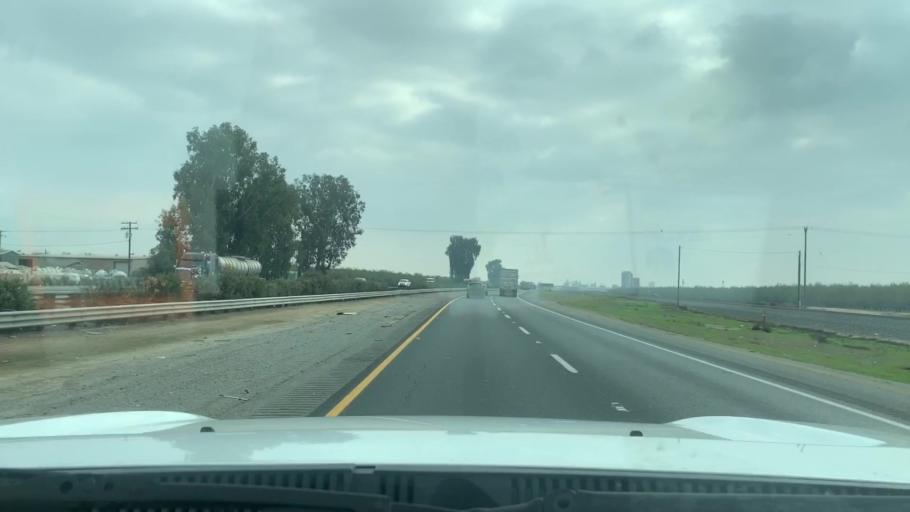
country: US
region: California
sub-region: Tulare County
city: Tipton
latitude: 36.0234
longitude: -119.3062
